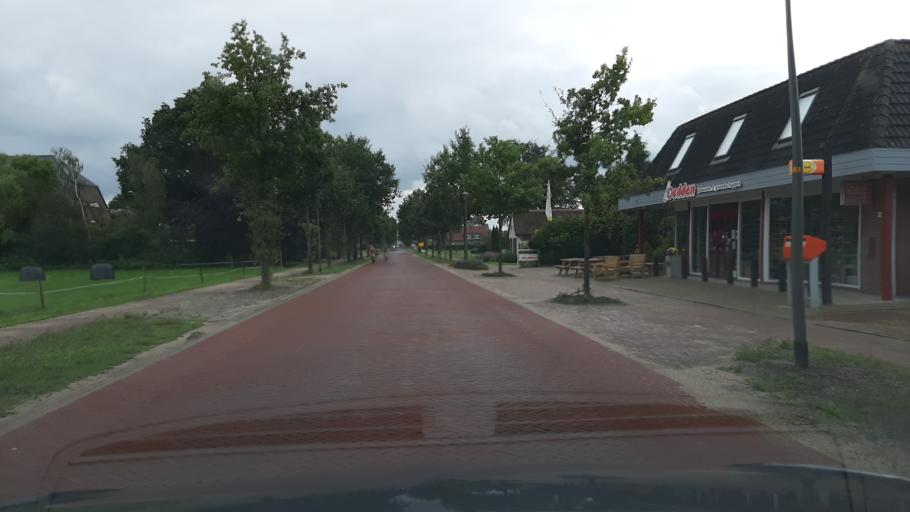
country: NL
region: Overijssel
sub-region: Gemeente Steenwijkerland
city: Steenwijkerwold
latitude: 52.8230
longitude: 6.0642
